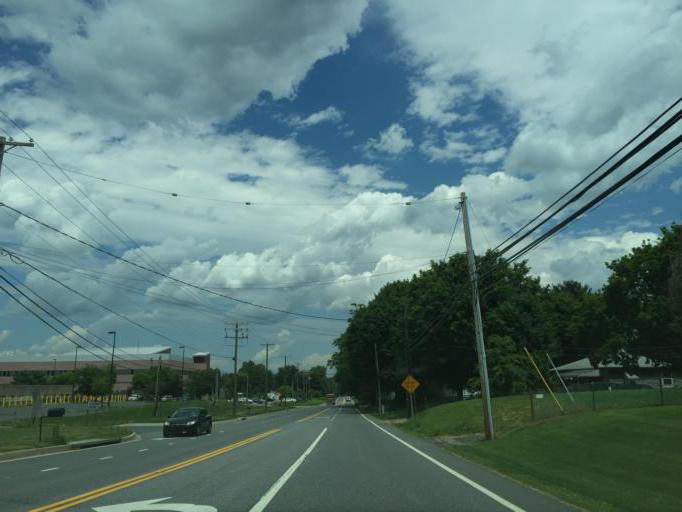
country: US
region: Maryland
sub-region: Harford County
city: Bel Air North
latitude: 39.5795
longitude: -76.3454
